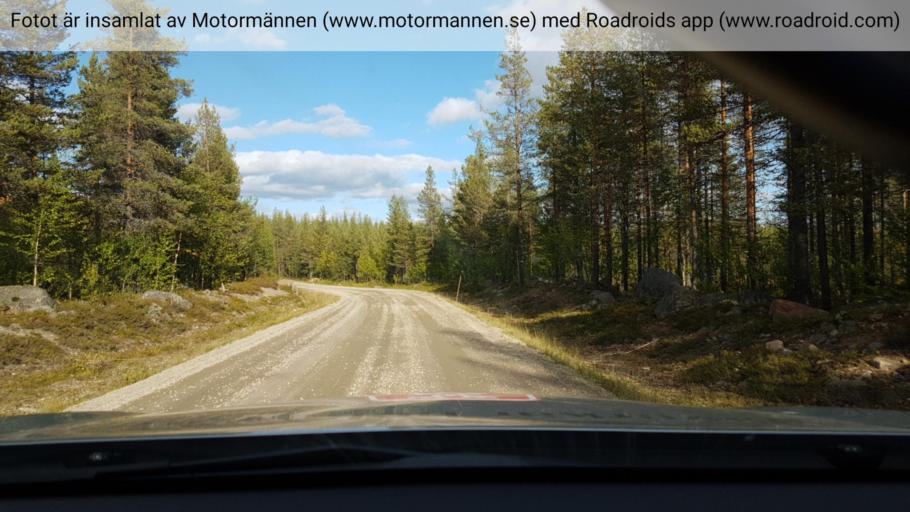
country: SE
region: Vaesterbotten
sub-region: Sorsele Kommun
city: Sorsele
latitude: 65.3542
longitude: 18.0126
